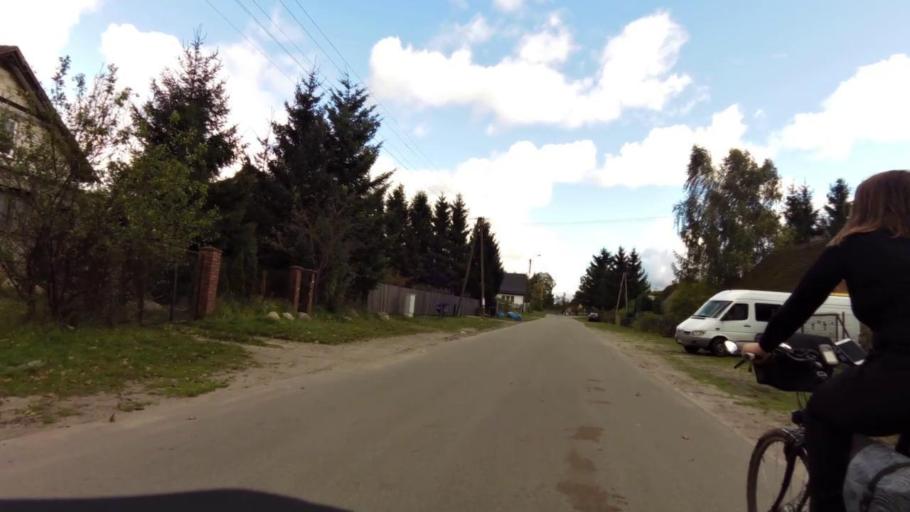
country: PL
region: West Pomeranian Voivodeship
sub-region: Powiat bialogardzki
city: Bialogard
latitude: 54.0375
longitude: 16.0558
